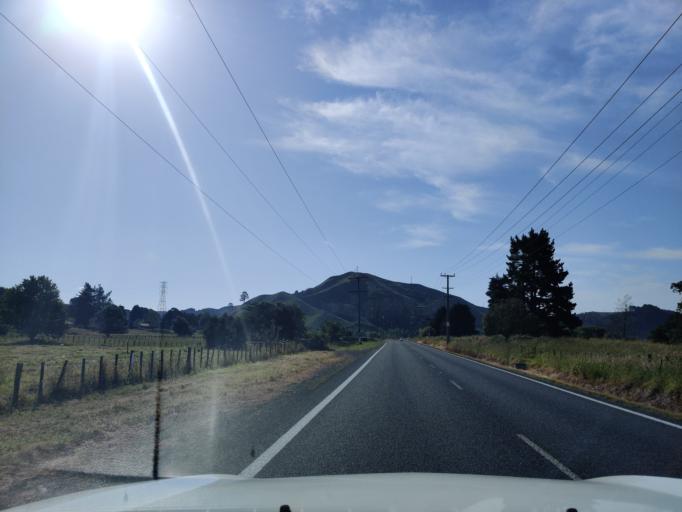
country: NZ
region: Waikato
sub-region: Waikato District
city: Ngaruawahia
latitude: -37.6036
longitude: 175.1667
